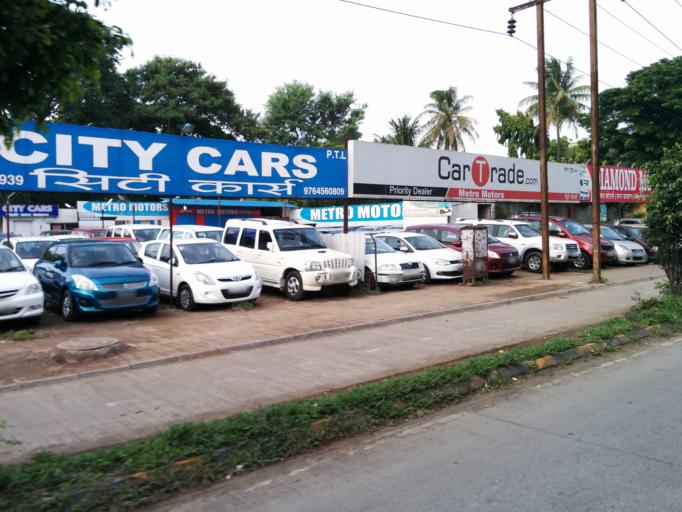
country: IN
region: Maharashtra
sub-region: Pune Division
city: Pune
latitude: 18.5064
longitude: 73.9042
